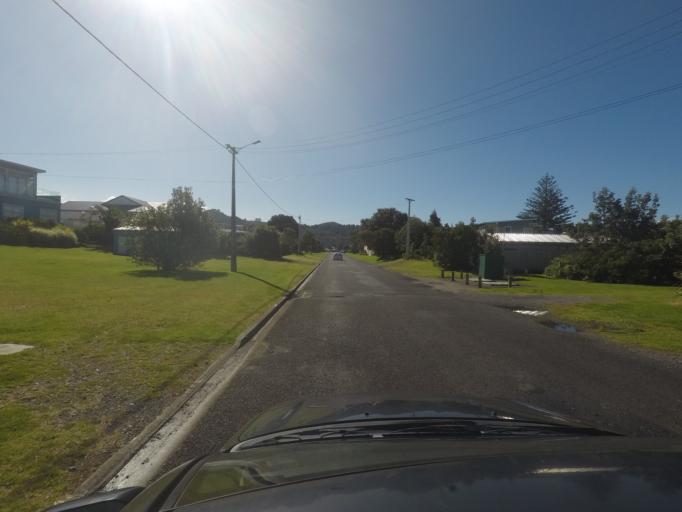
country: NZ
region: Bay of Plenty
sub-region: Western Bay of Plenty District
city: Waihi Beach
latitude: -37.4076
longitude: 175.9441
